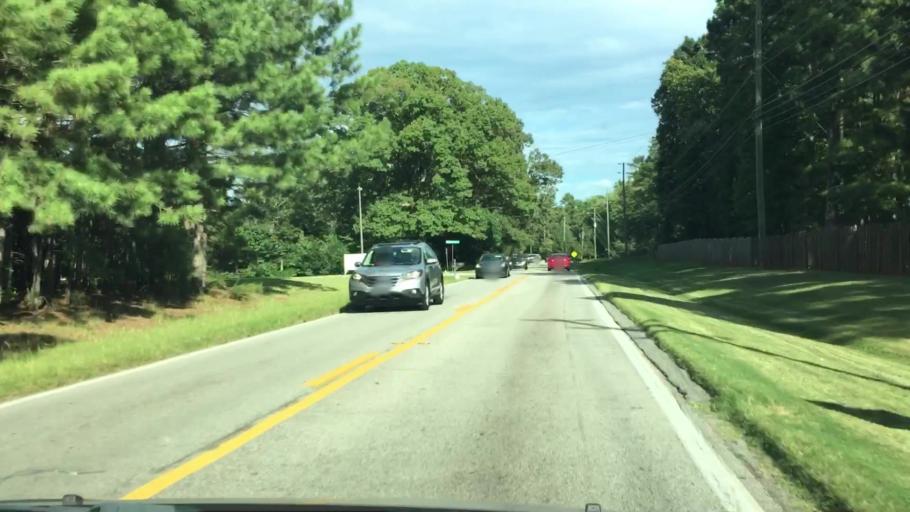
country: US
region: Georgia
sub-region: Henry County
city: Stockbridge
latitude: 33.6058
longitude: -84.2161
